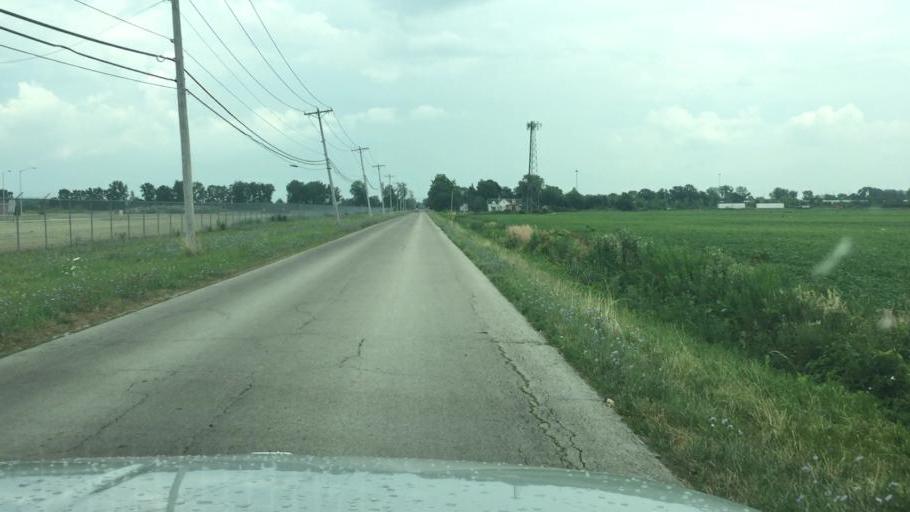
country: US
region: Ohio
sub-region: Wood County
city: Walbridge
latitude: 41.5879
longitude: -83.5257
